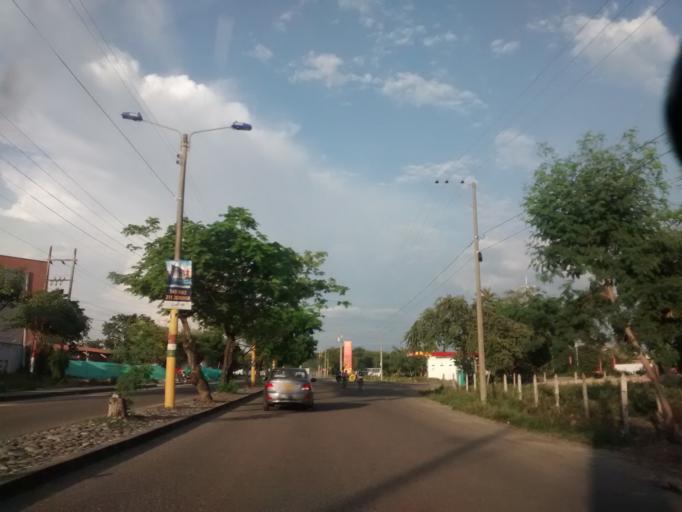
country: CO
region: Cundinamarca
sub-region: Girardot
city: Girardot City
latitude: 4.3043
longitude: -74.8143
